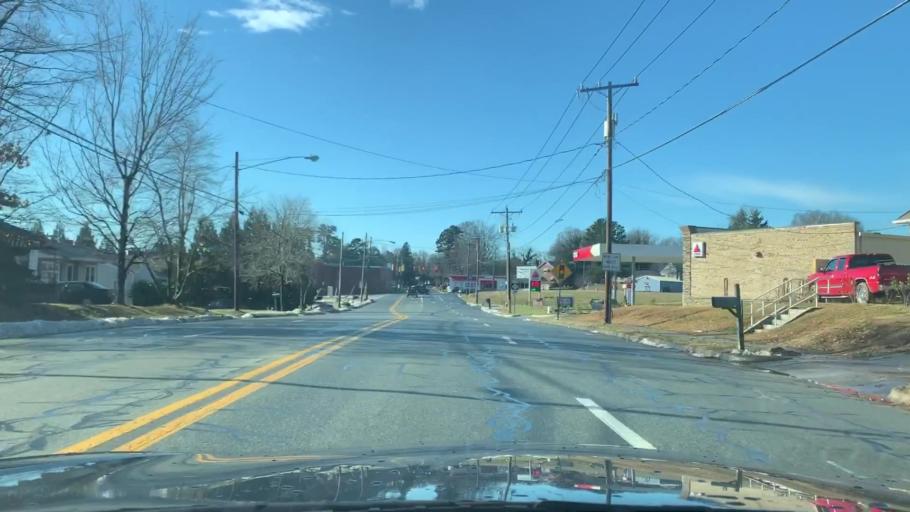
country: US
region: North Carolina
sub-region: Alamance County
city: Graham
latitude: 36.0717
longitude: -79.3927
